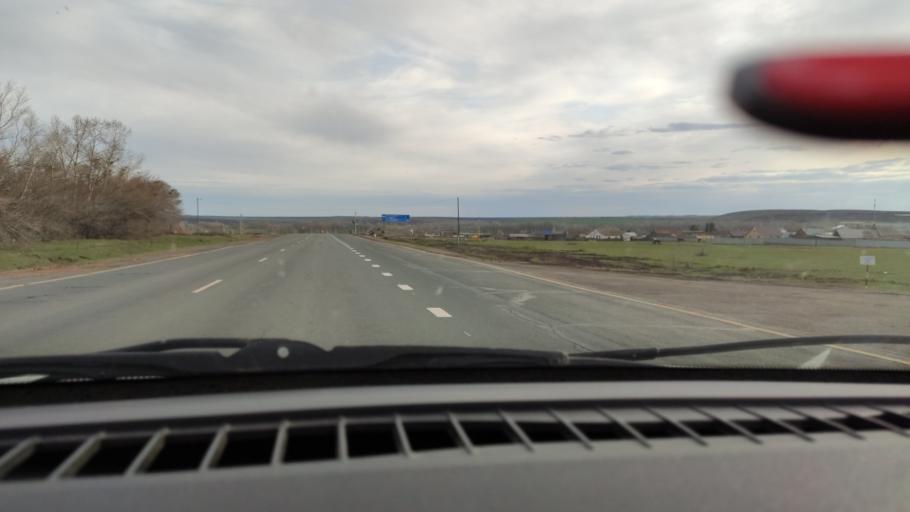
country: RU
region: Orenburg
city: Sakmara
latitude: 52.2147
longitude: 55.3248
